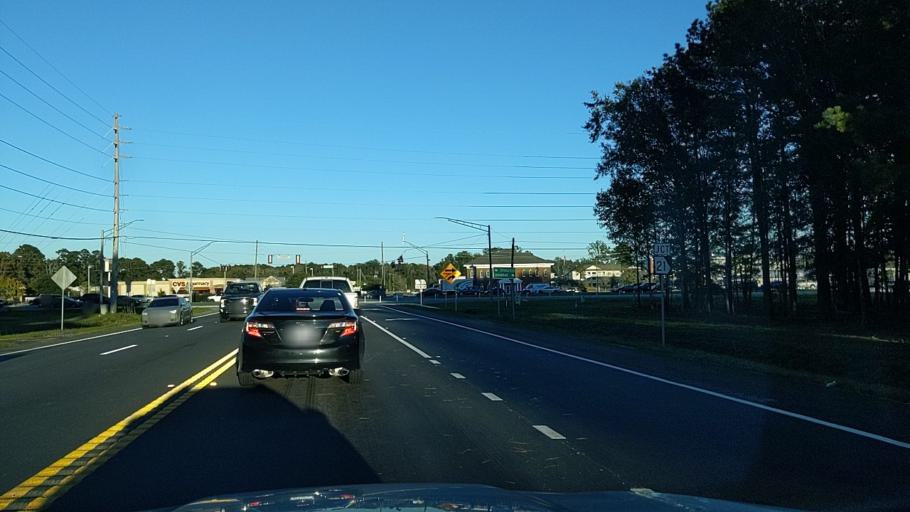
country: US
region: Georgia
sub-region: Chatham County
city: Port Wentworth
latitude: 32.1981
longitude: -81.1988
